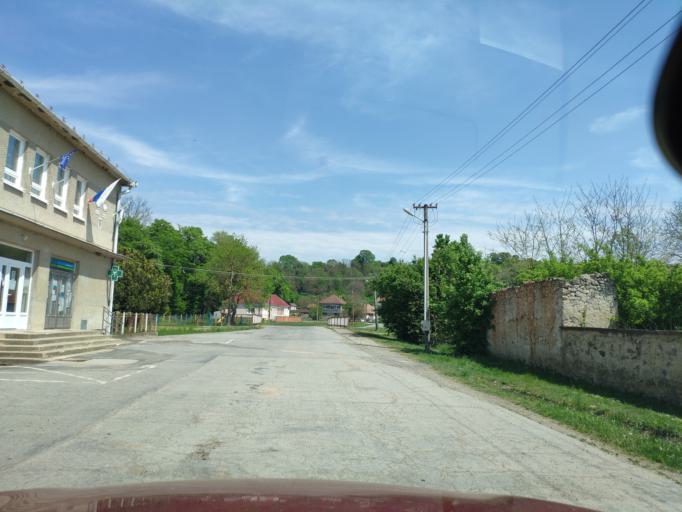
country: SK
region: Banskobystricky
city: Rimavska Sobota
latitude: 48.4470
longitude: 20.1145
